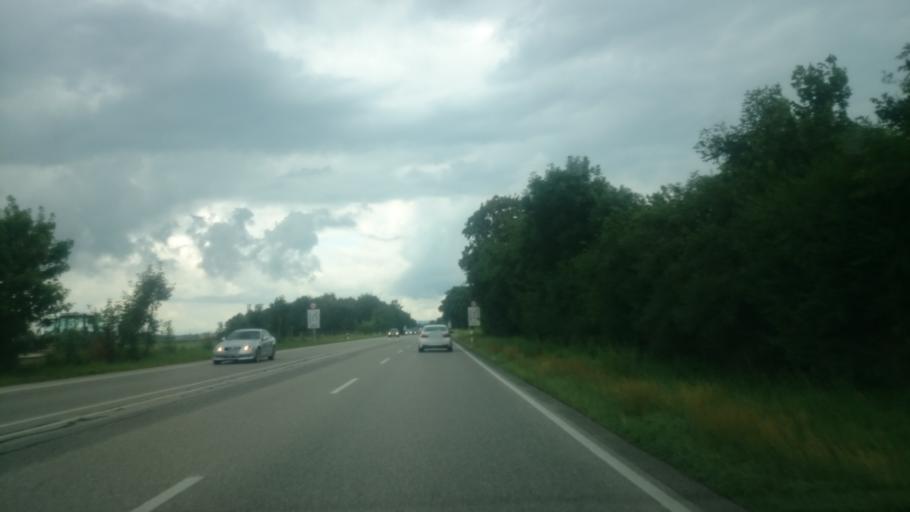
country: DE
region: Bavaria
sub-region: Swabia
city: Rieden
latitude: 47.9510
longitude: 10.6757
